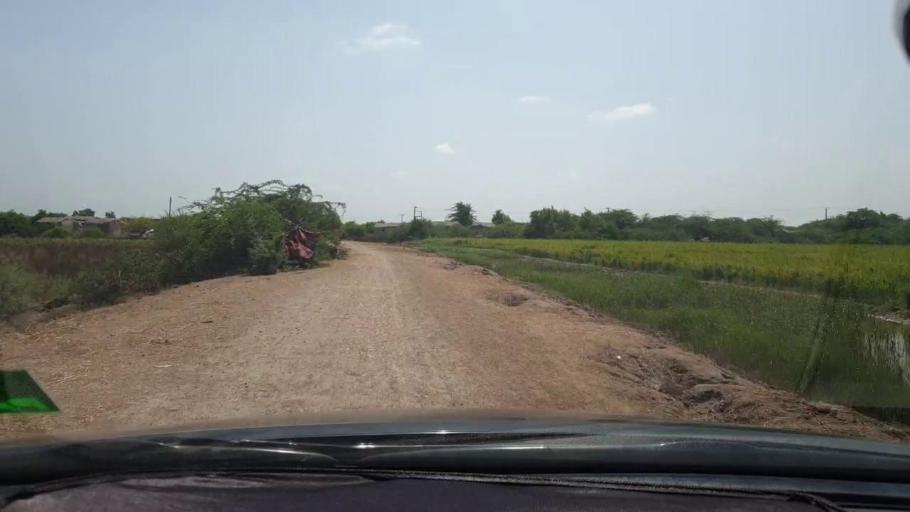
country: PK
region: Sindh
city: Tando Bago
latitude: 24.8881
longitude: 69.1012
